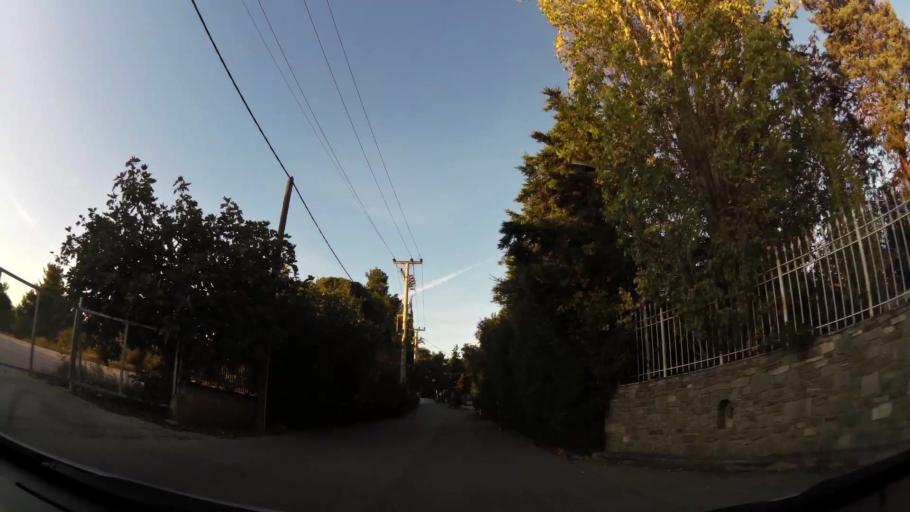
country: GR
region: Attica
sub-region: Nomarchia Anatolikis Attikis
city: Kryoneri
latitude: 38.1371
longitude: 23.8367
